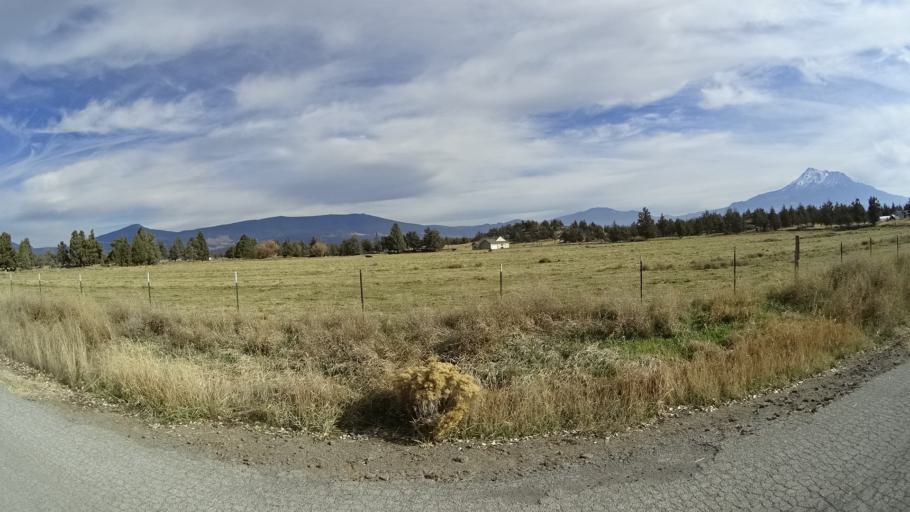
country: US
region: California
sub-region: Siskiyou County
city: Montague
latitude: 41.6085
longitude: -122.4048
